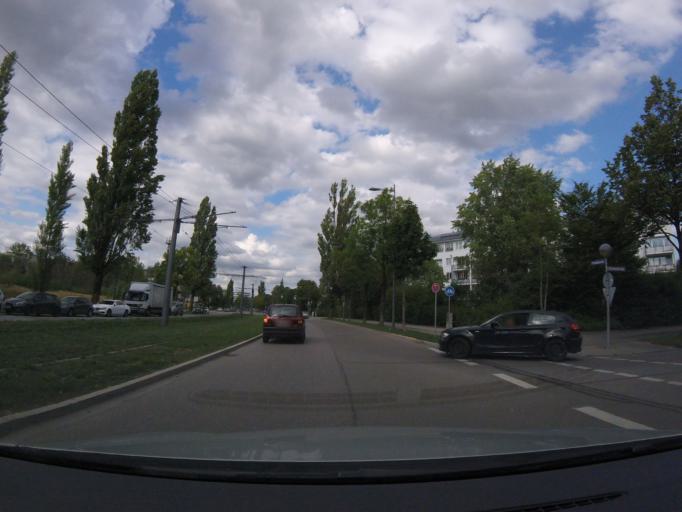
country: DE
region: Bavaria
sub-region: Upper Bavaria
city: Bogenhausen
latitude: 48.1682
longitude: 11.6336
